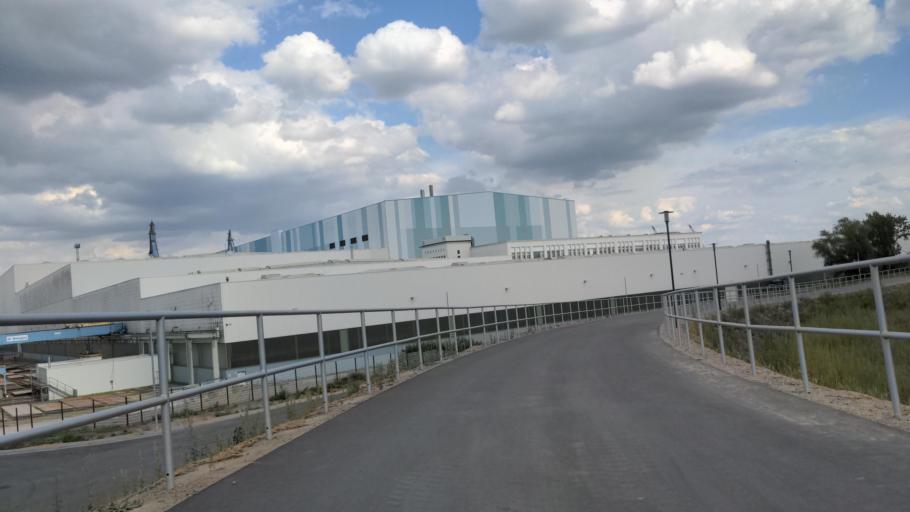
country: DE
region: Mecklenburg-Vorpommern
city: Wismar
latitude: 53.8981
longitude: 11.4304
